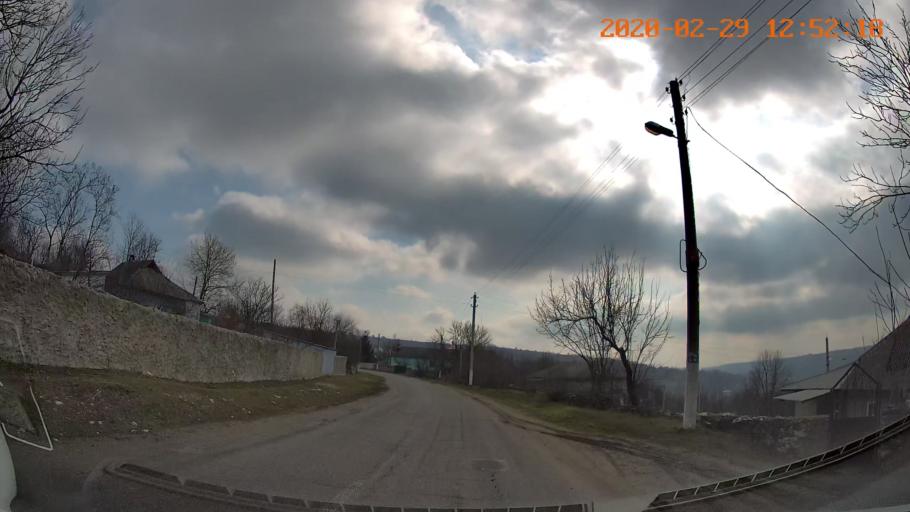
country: MD
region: Telenesti
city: Camenca
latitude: 48.1125
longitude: 28.7327
